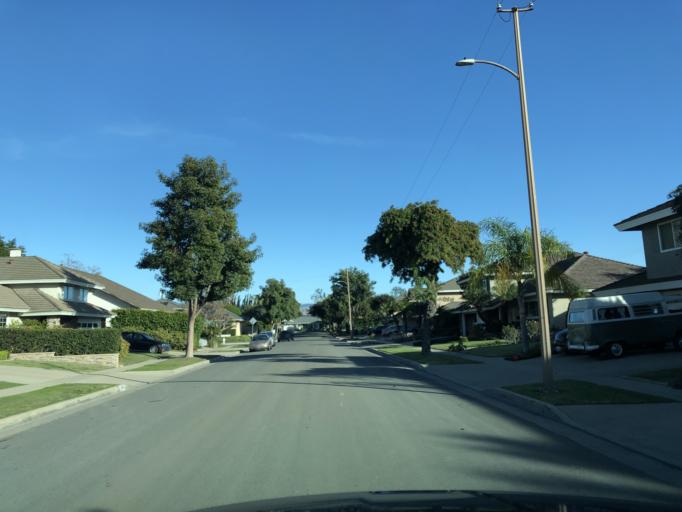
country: US
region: California
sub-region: Orange County
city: Tustin
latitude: 33.7639
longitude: -117.8410
